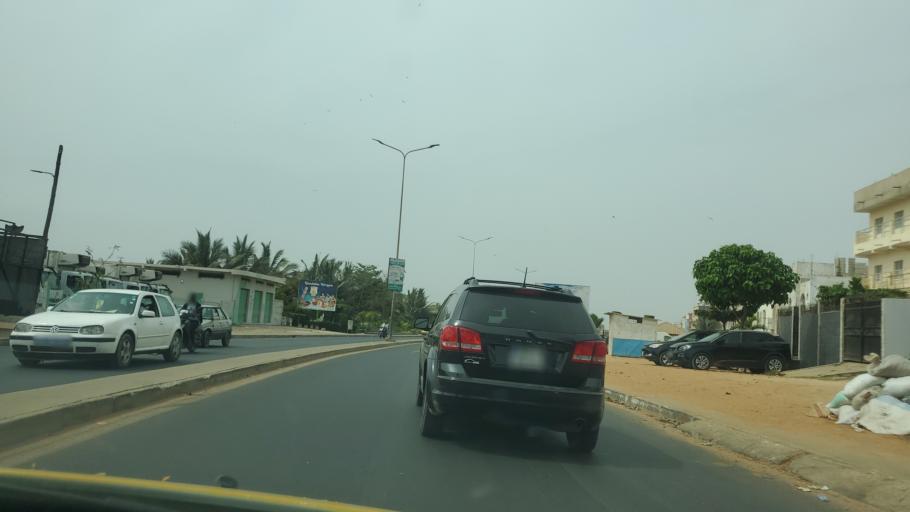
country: SN
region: Dakar
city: Pikine
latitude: 14.7506
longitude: -17.4081
